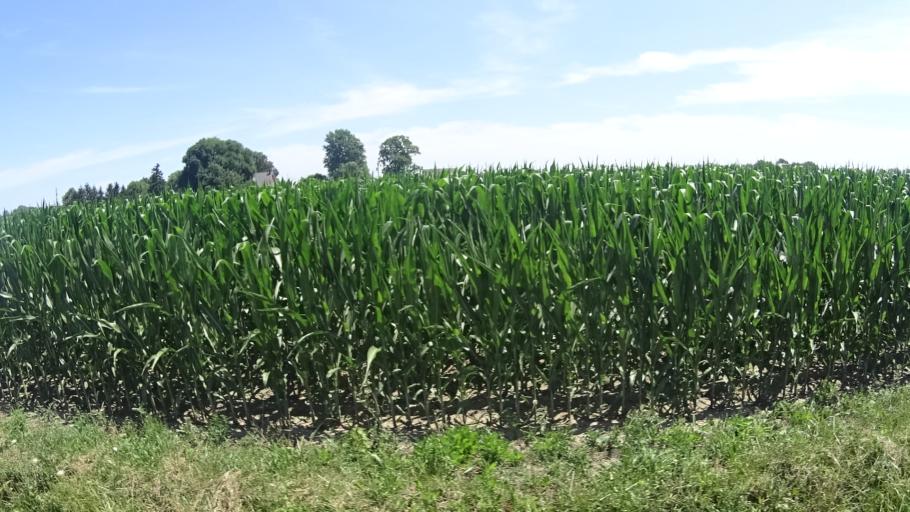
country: US
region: Ohio
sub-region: Erie County
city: Sandusky
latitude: 41.4286
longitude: -82.7922
